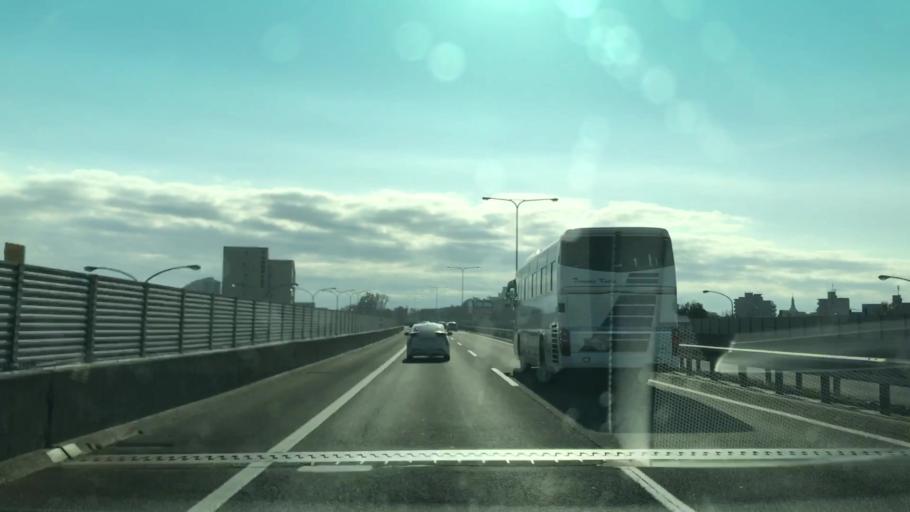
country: JP
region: Hokkaido
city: Sapporo
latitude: 43.0318
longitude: 141.4449
